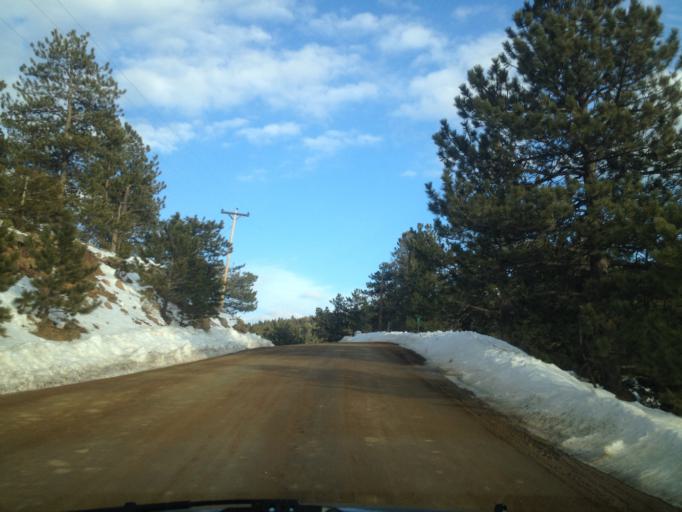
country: US
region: Colorado
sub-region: Boulder County
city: Nederland
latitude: 40.1222
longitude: -105.4505
